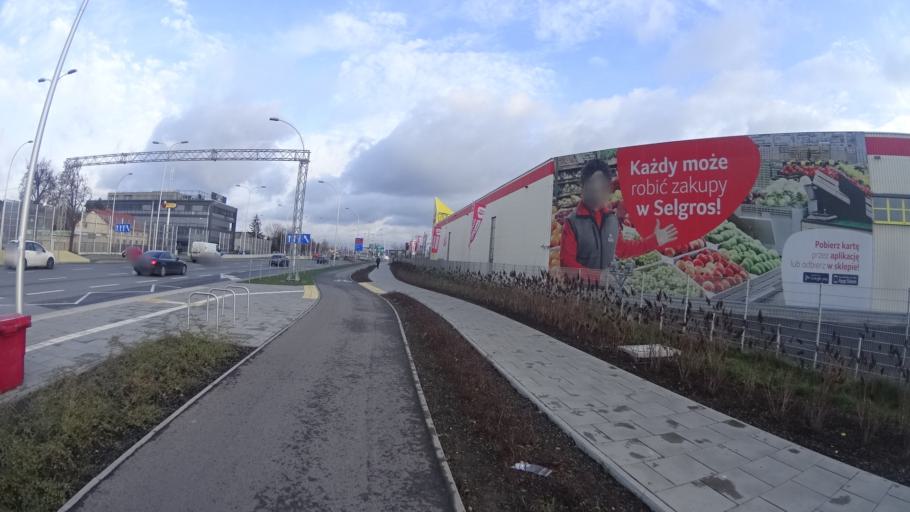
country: PL
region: Masovian Voivodeship
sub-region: Warszawa
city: Ursus
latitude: 52.2161
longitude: 20.8916
